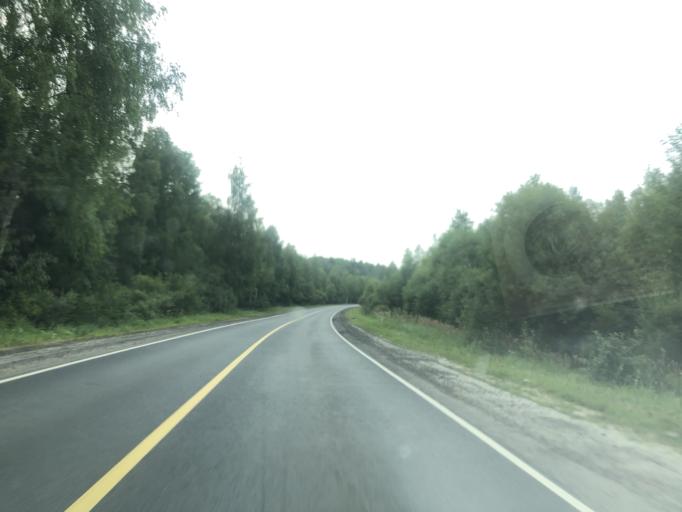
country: RU
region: Ivanovo
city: Verkhniy Landekh
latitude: 56.7735
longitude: 42.4007
